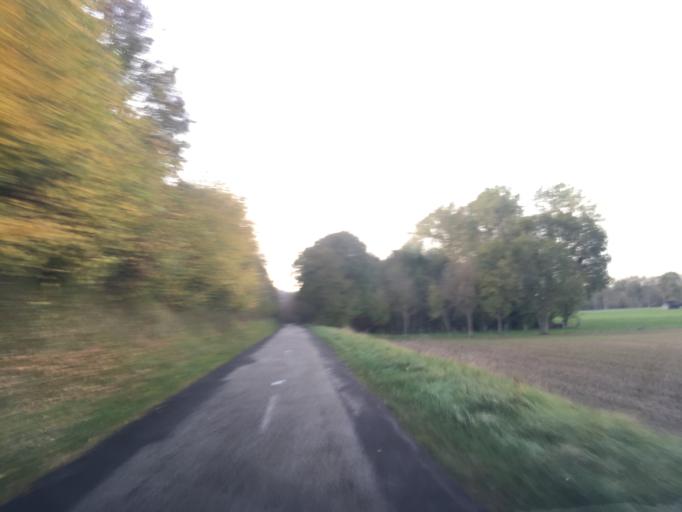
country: FR
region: Haute-Normandie
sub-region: Departement de l'Eure
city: Heudreville-sur-Eure
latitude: 49.1038
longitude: 1.2279
